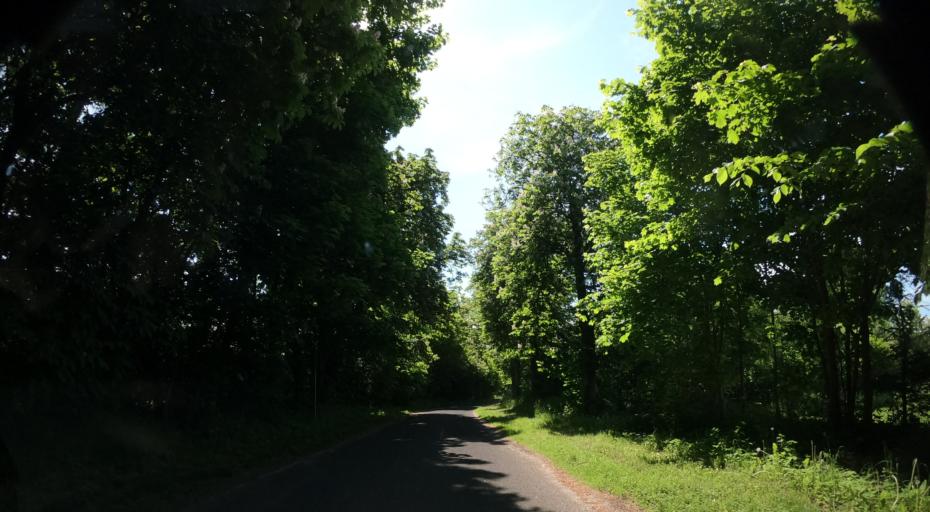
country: PL
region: West Pomeranian Voivodeship
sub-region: Powiat kolobrzeski
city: Ustronie Morskie
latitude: 54.1631
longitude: 15.8094
